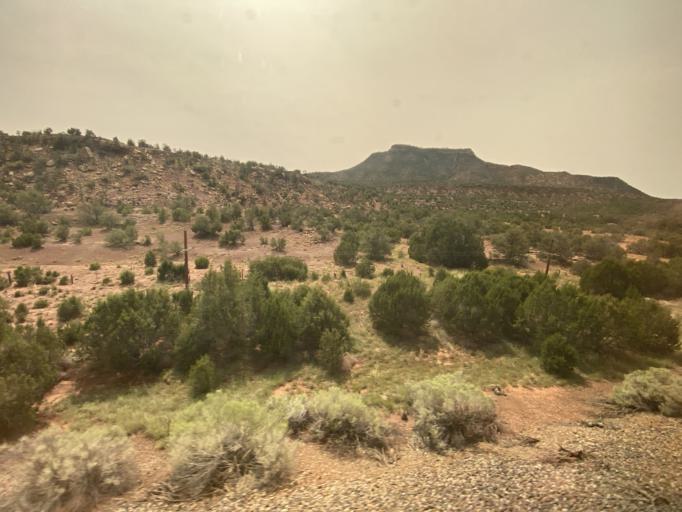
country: US
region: New Mexico
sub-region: San Miguel County
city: Pecos
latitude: 35.4036
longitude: -105.4987
